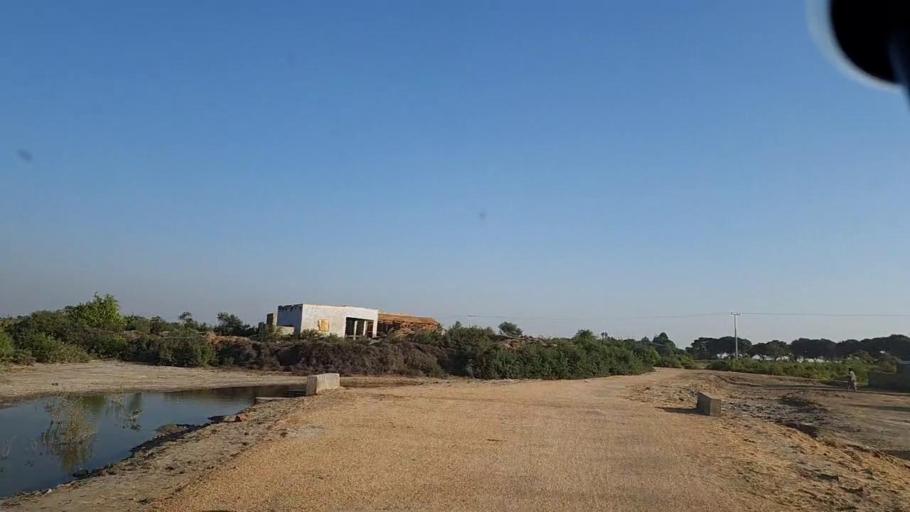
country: PK
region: Sindh
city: Chuhar Jamali
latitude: 24.5613
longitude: 68.0751
